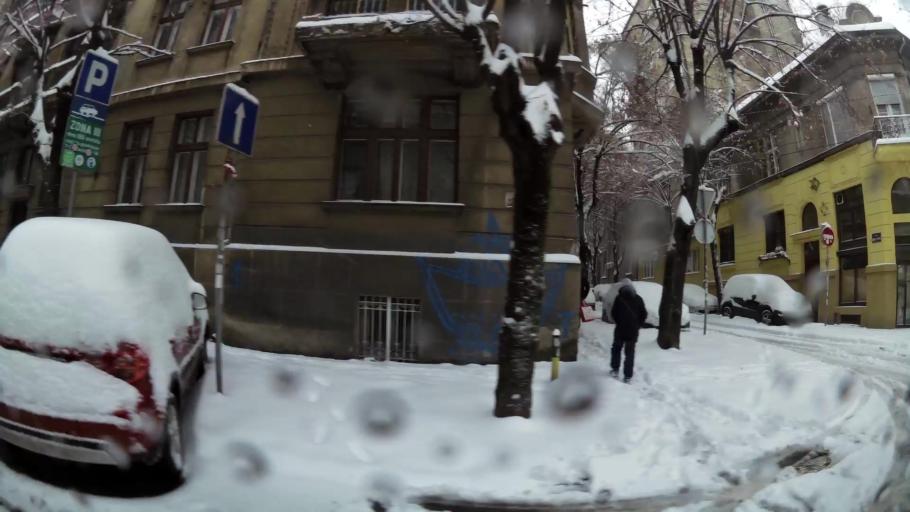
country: RS
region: Central Serbia
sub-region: Belgrade
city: Stari Grad
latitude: 44.8228
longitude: 20.4629
